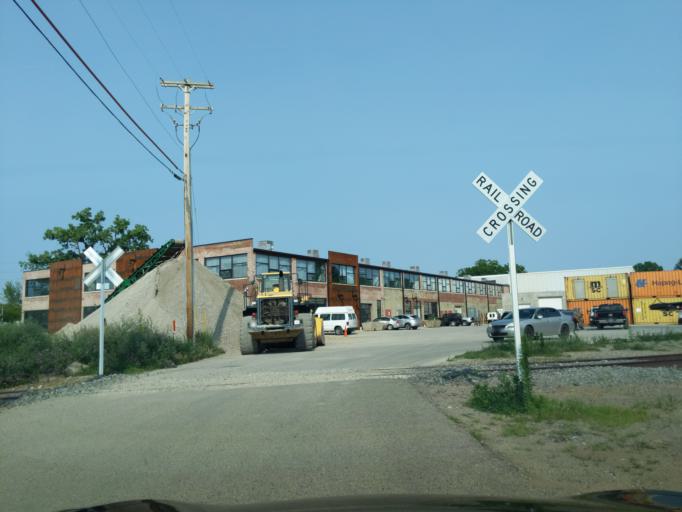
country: US
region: Michigan
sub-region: Ingham County
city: Lansing
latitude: 42.7201
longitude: -84.5427
